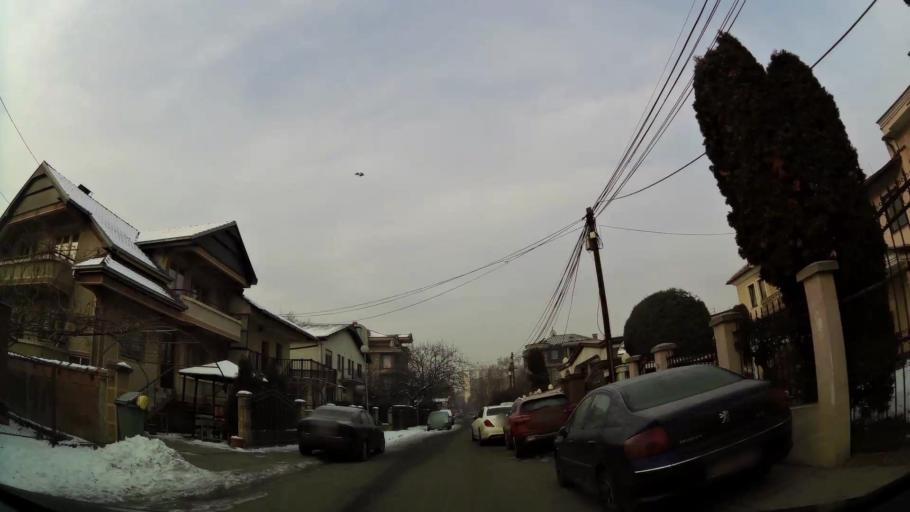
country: MK
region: Butel
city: Butel
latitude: 42.0233
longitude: 21.4459
